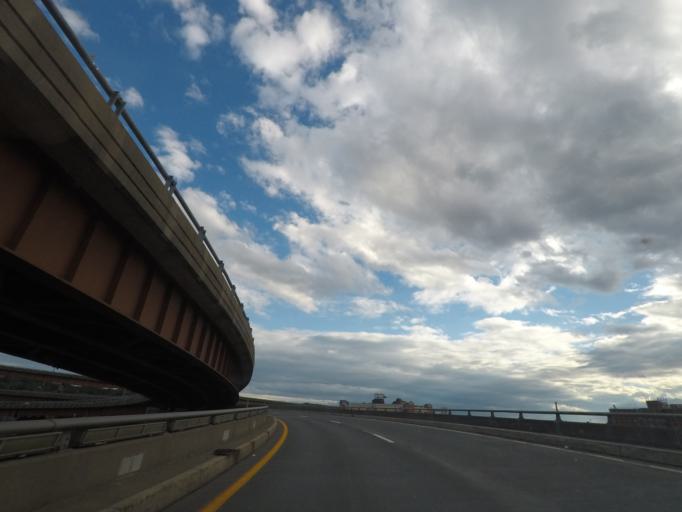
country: US
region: New York
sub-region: Rensselaer County
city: Rensselaer
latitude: 42.6437
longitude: -73.7521
